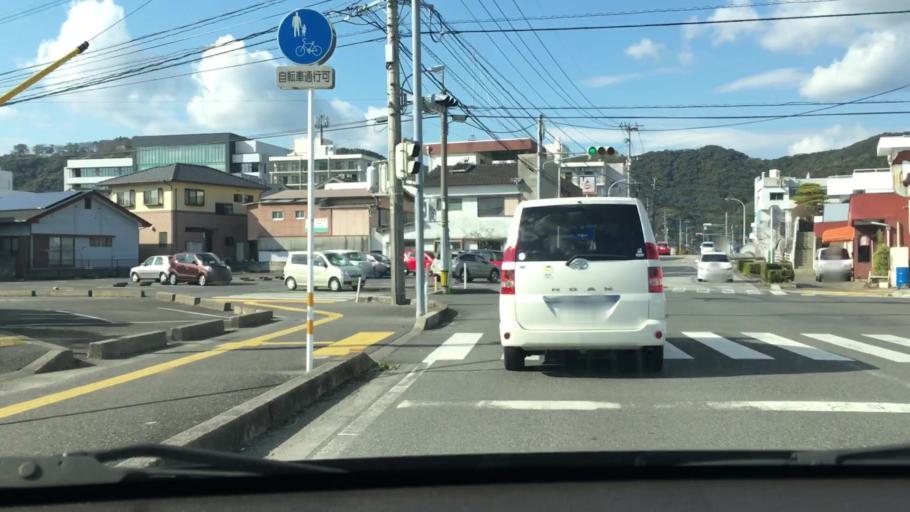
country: JP
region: Oita
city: Saiki
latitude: 32.9595
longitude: 131.9028
